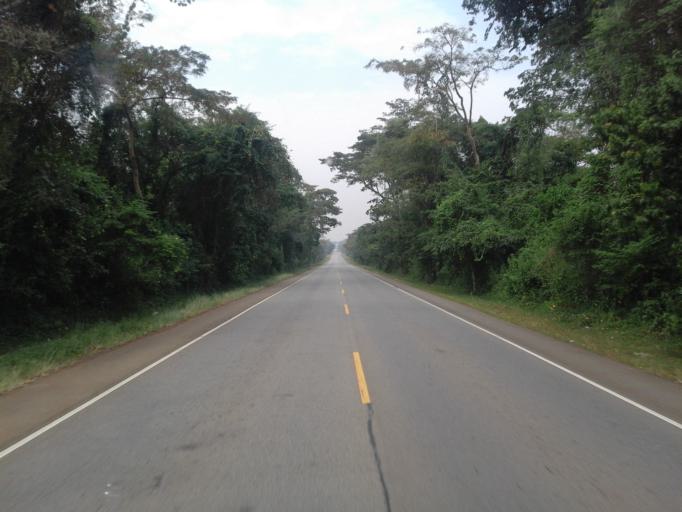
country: UG
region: Eastern Region
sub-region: Busia District
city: Busia
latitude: 0.5297
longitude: 33.9812
